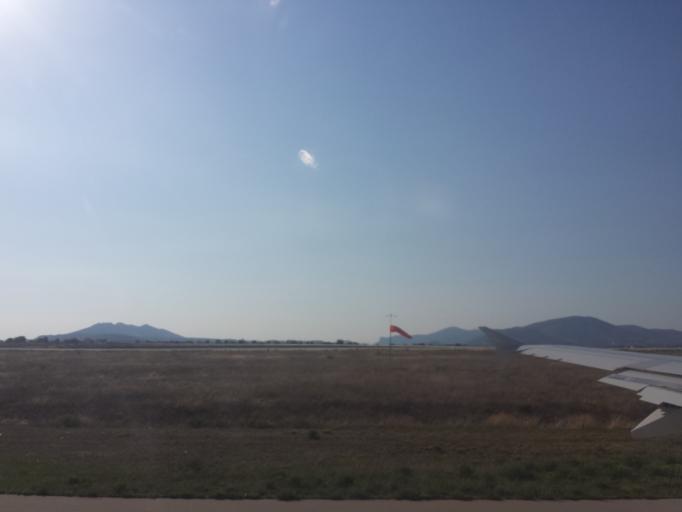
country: GR
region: Attica
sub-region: Nomarchia Anatolikis Attikis
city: Spata
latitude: 37.9281
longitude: 23.9447
